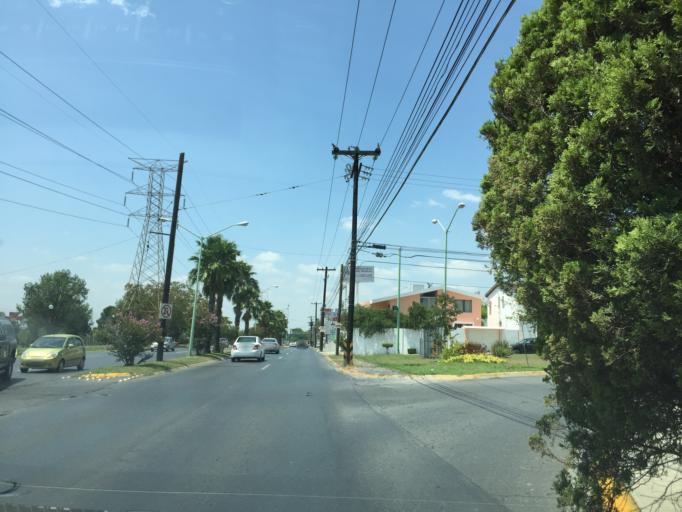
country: MX
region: Nuevo Leon
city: Guadalupe
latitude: 25.6443
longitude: -100.2682
